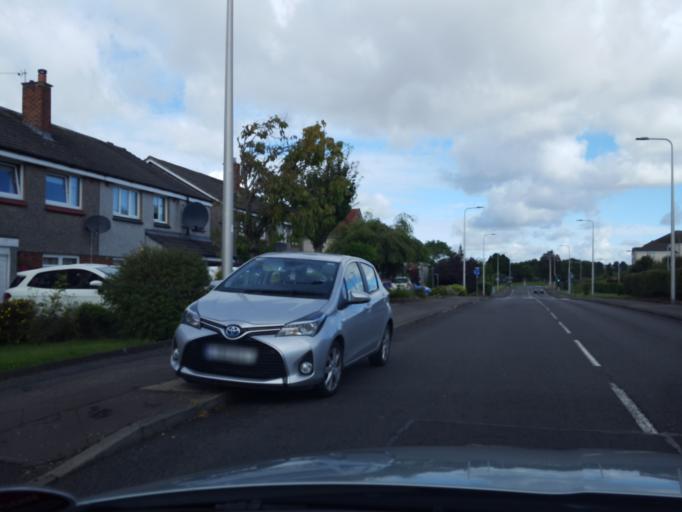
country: GB
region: Scotland
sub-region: Fife
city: Rosyth
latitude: 56.0575
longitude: -3.4155
